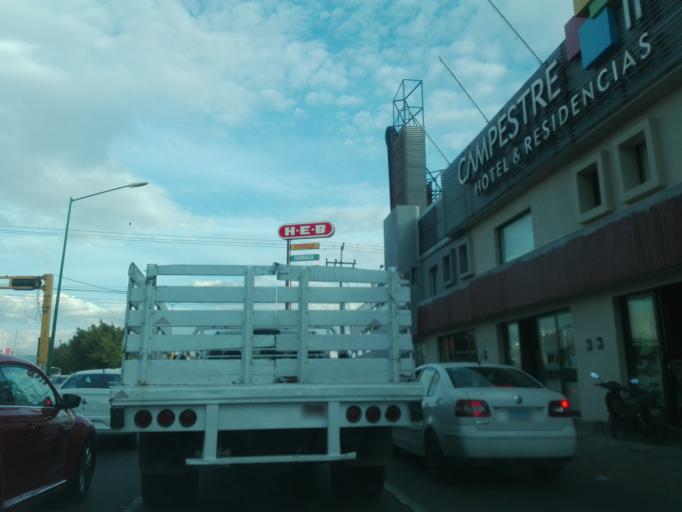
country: MX
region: Guanajuato
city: Leon
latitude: 21.1473
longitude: -101.6857
